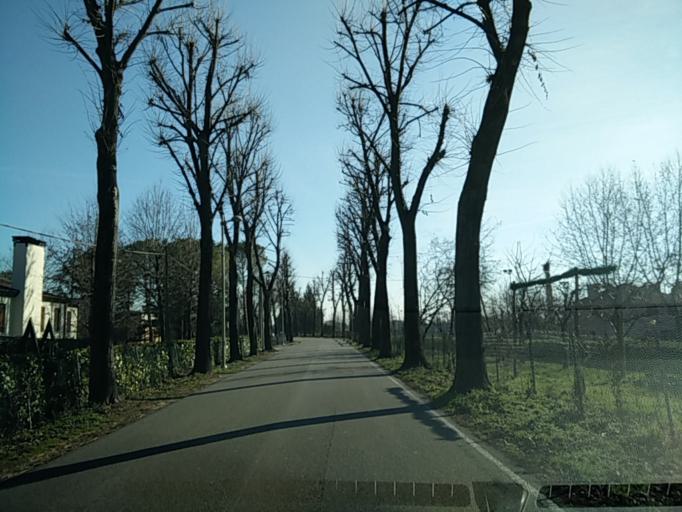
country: IT
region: Veneto
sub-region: Provincia di Treviso
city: San Vendemiano-Fossamerlo
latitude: 45.8903
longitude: 12.3363
